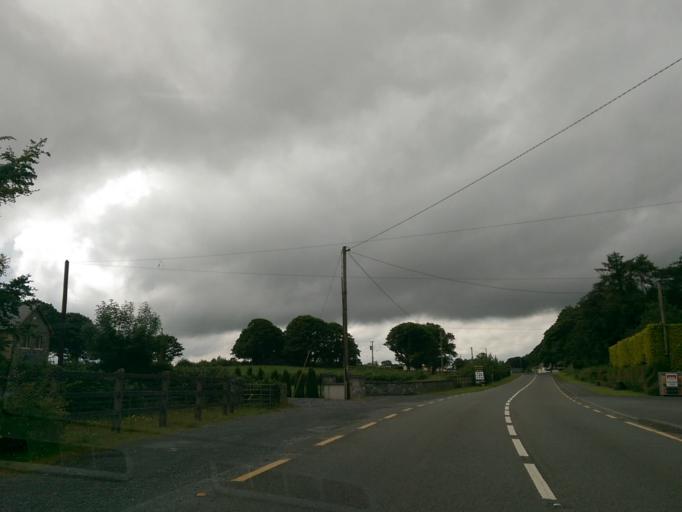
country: IE
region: Munster
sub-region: An Clar
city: Ennis
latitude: 52.7424
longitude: -9.1624
